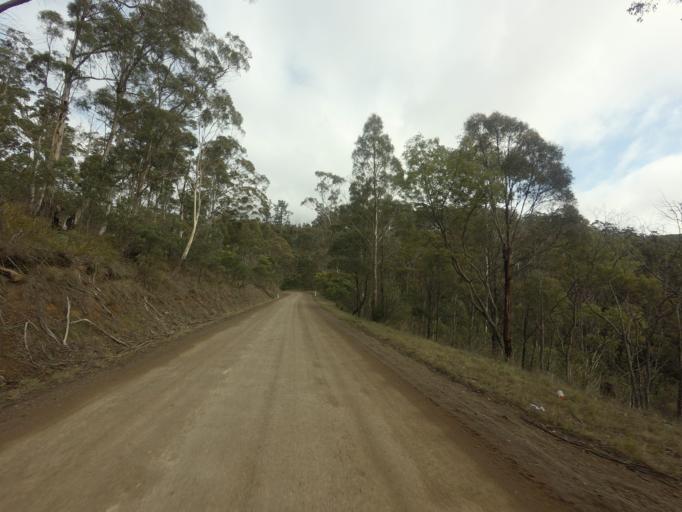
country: AU
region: Tasmania
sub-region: Derwent Valley
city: New Norfolk
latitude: -42.7507
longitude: 146.8715
